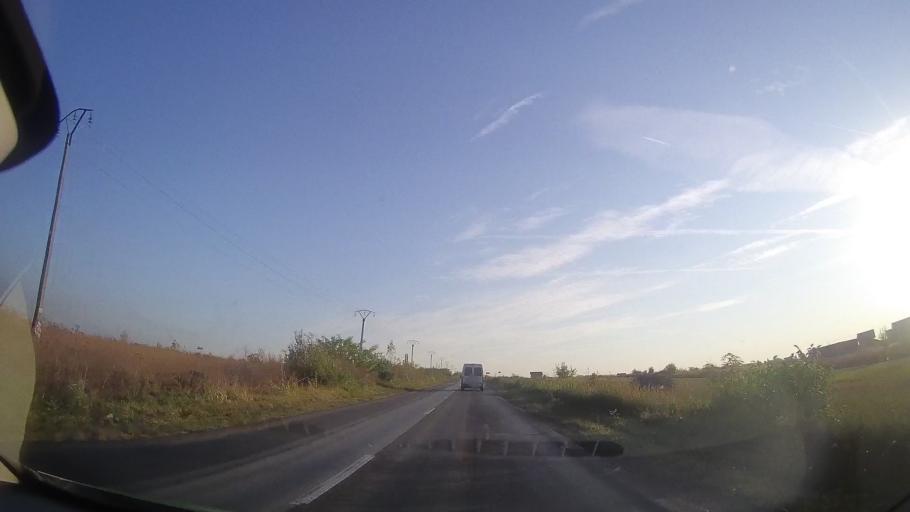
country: RO
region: Timis
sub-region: Comuna Giarmata
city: Giarmata
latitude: 45.8415
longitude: 21.2981
